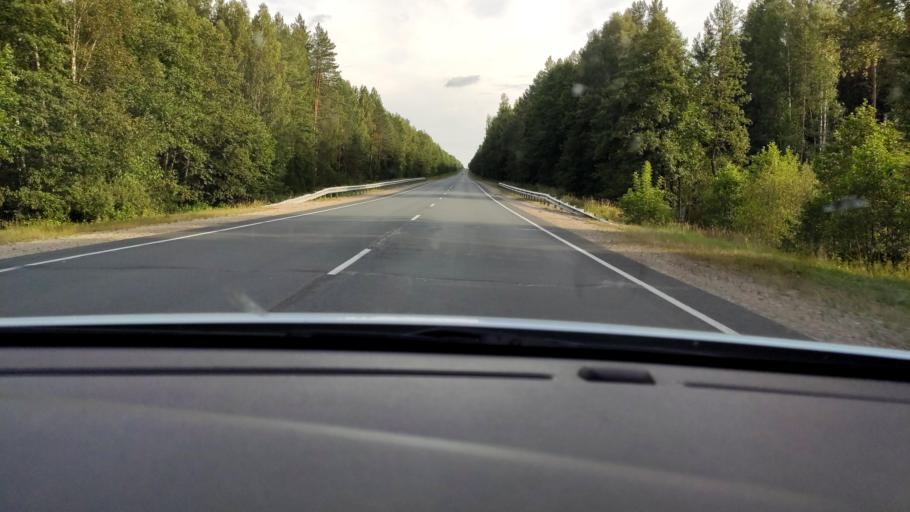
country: RU
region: Mariy-El
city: Suslonger
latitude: 56.2752
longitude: 48.2331
